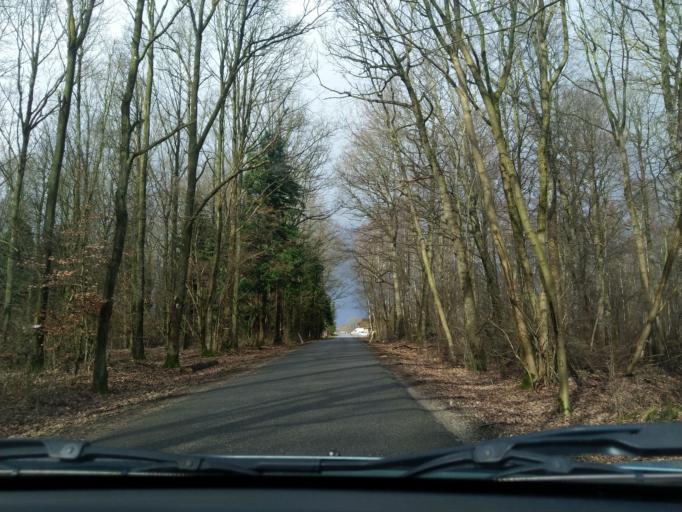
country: DK
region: Zealand
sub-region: Naestved Kommune
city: Fuglebjerg
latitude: 55.3334
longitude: 11.5820
